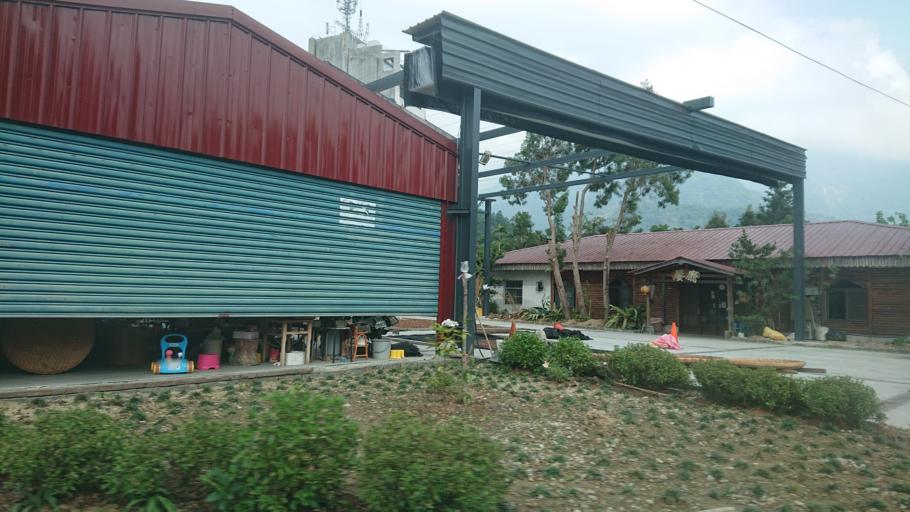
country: TW
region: Taiwan
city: Lugu
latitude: 23.5810
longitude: 120.6938
